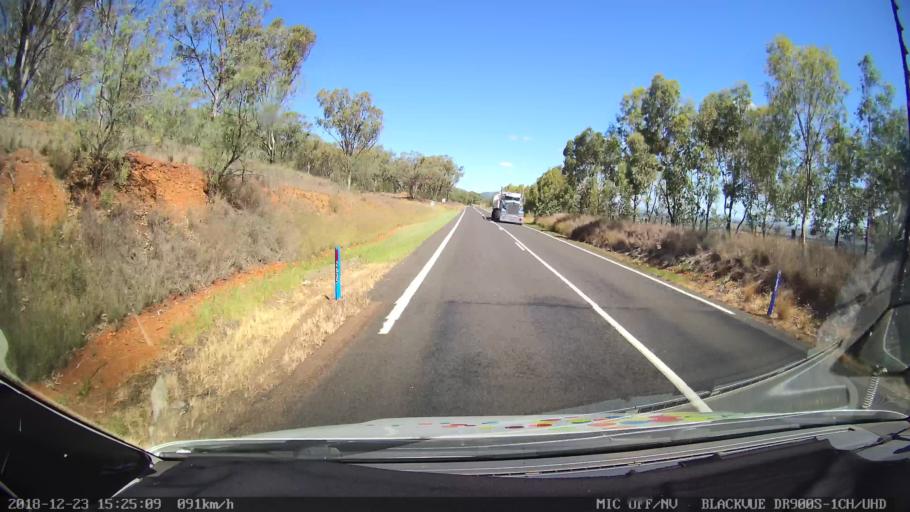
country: AU
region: New South Wales
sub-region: Tamworth Municipality
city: Manilla
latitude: -30.9006
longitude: 150.8279
